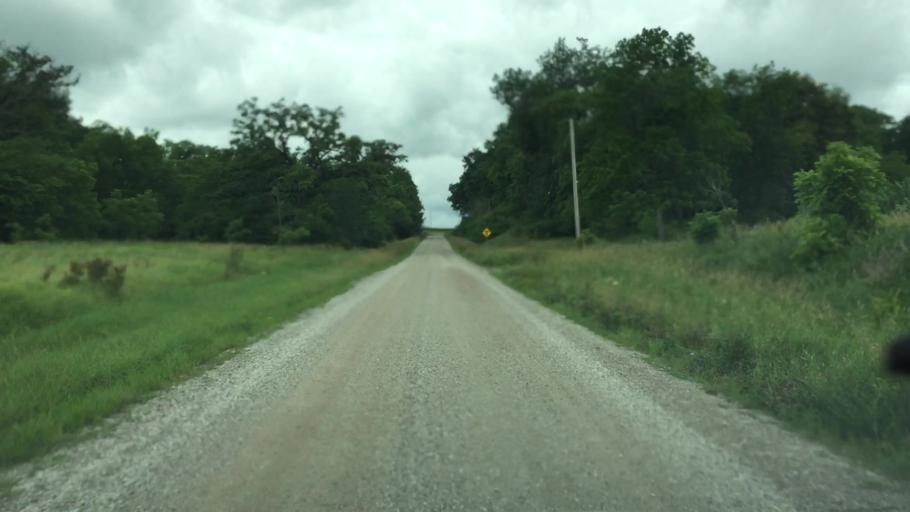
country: US
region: Iowa
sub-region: Jasper County
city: Monroe
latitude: 41.5952
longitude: -93.1119
